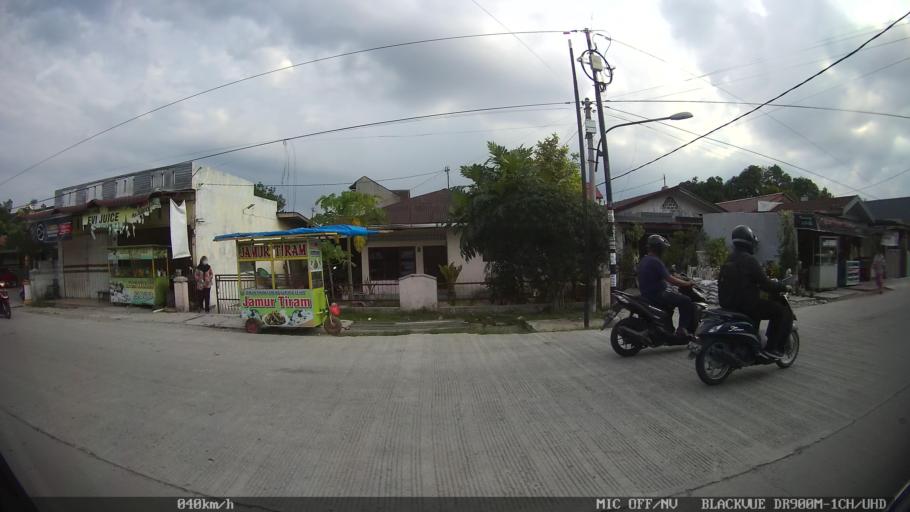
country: ID
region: North Sumatra
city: Sunggal
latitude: 3.5623
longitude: 98.6239
